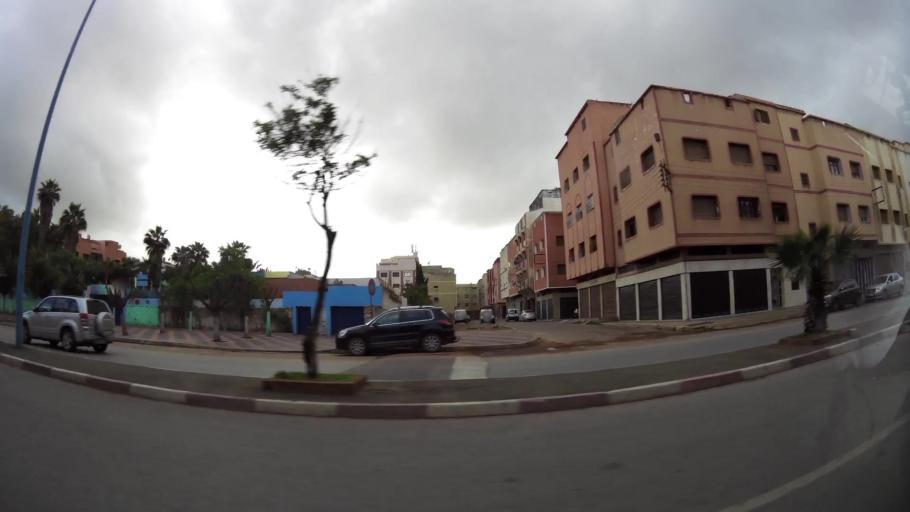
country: MA
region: Grand Casablanca
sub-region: Casablanca
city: Casablanca
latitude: 33.5435
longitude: -7.5885
